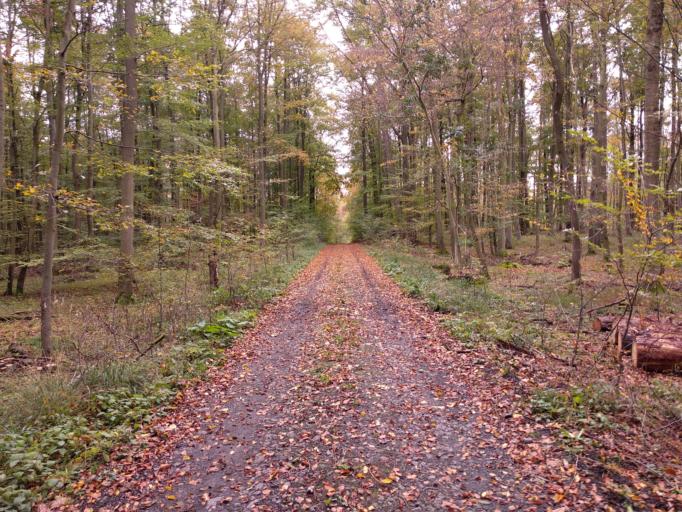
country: DE
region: North Rhine-Westphalia
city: Beverungen
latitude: 51.6654
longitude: 9.3305
